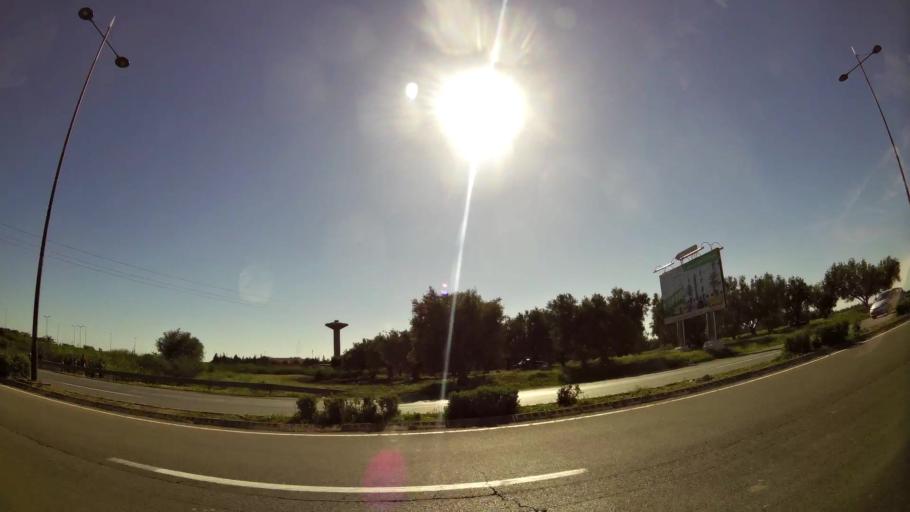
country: MA
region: Fes-Boulemane
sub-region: Fes
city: Fes
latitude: 33.9932
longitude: -5.0240
